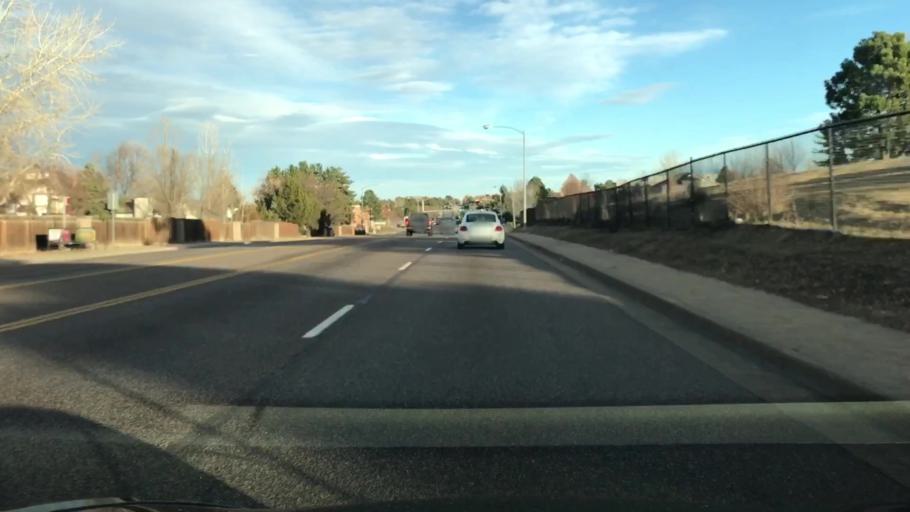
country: US
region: Colorado
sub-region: Adams County
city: Aurora
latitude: 39.6748
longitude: -104.8521
